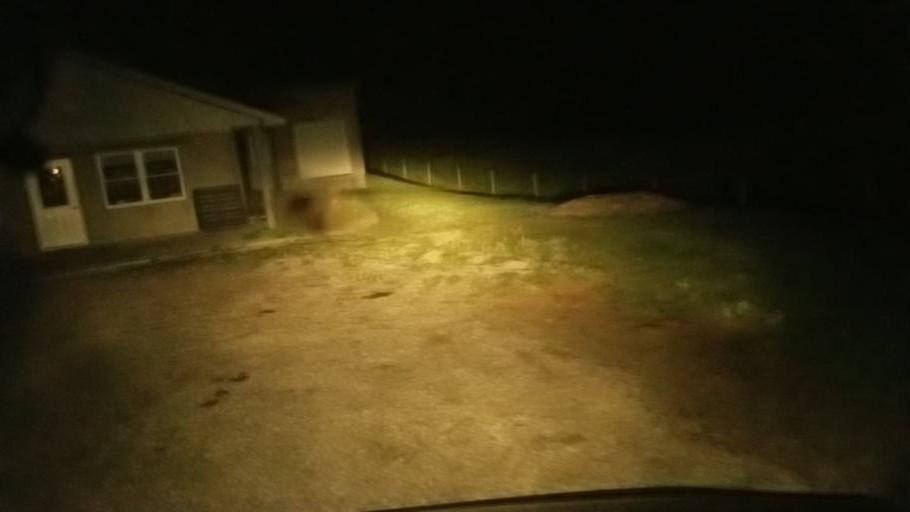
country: US
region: Ohio
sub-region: Knox County
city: Oak Hill
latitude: 40.4923
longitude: -82.1278
